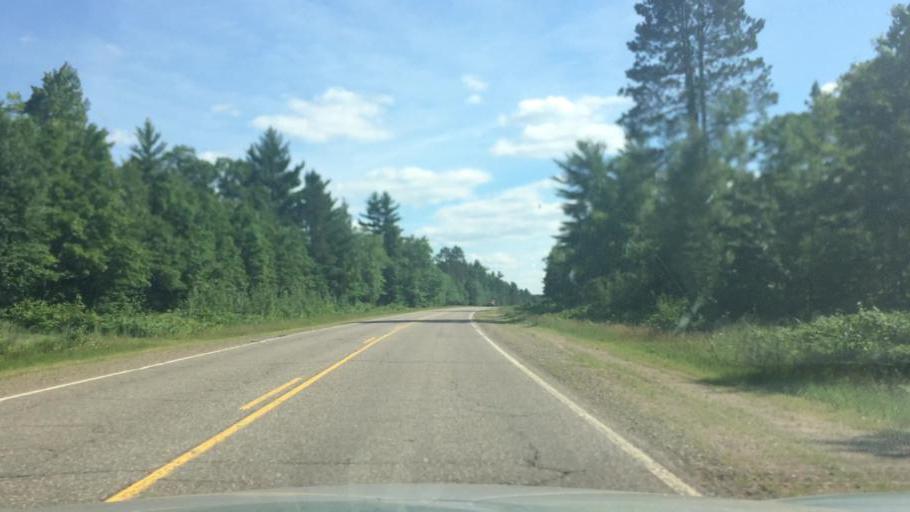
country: US
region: Wisconsin
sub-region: Vilas County
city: Lac du Flambeau
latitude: 46.0767
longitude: -89.6443
